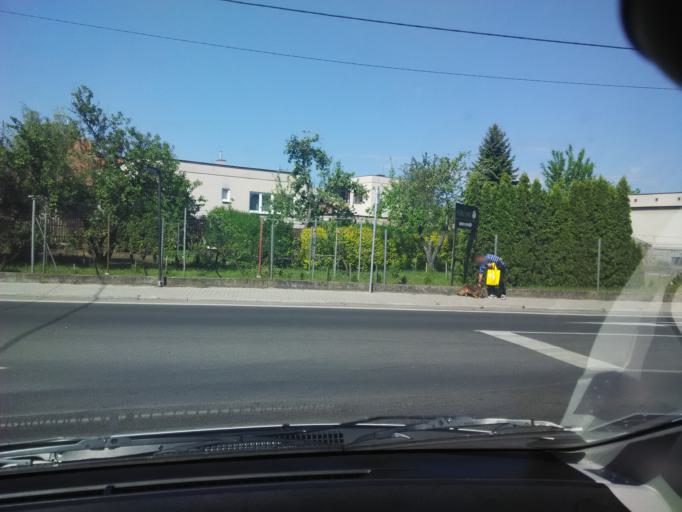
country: SK
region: Nitriansky
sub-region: Okres Nitra
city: Nitra
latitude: 48.2703
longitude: 18.1012
